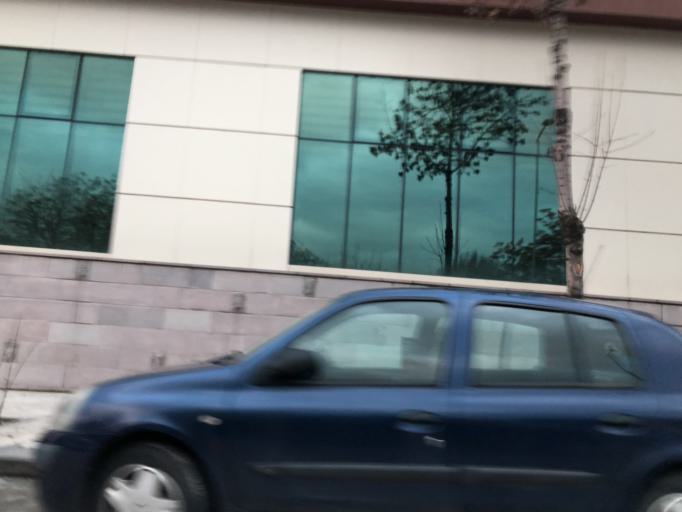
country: TR
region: Ankara
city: Ankara
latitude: 39.9622
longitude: 32.8110
